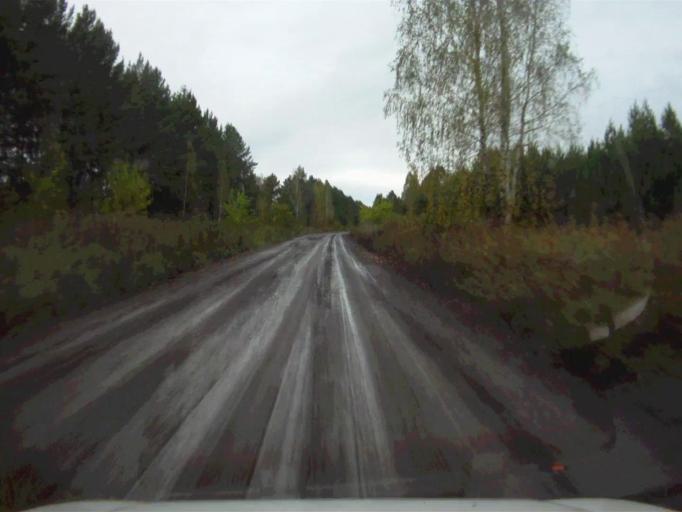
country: RU
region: Chelyabinsk
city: Nyazepetrovsk
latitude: 56.1401
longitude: 59.2956
